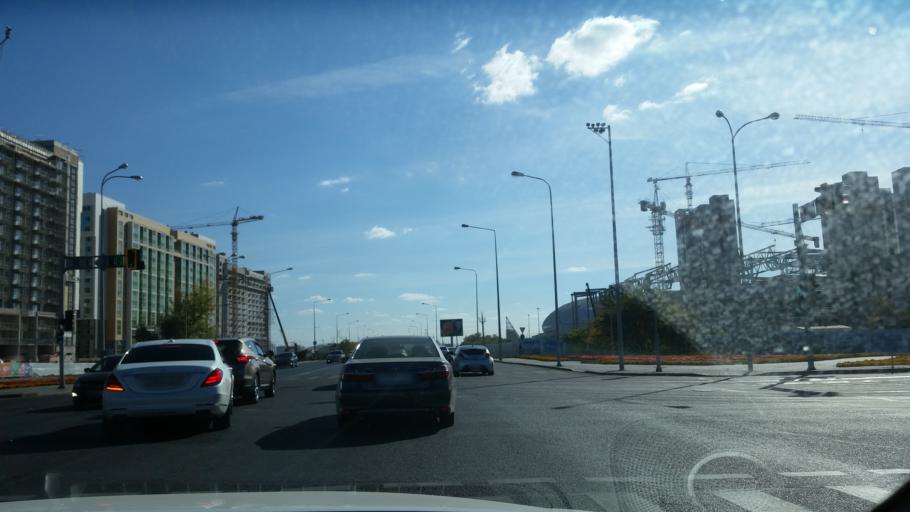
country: KZ
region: Astana Qalasy
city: Astana
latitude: 51.1164
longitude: 71.4114
